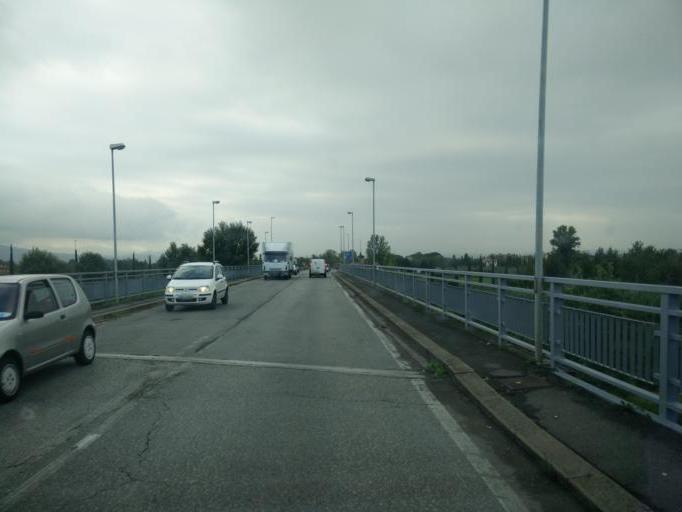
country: IT
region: Tuscany
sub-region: Province of Florence
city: Campi Bisenzio
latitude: 43.8325
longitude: 11.1337
